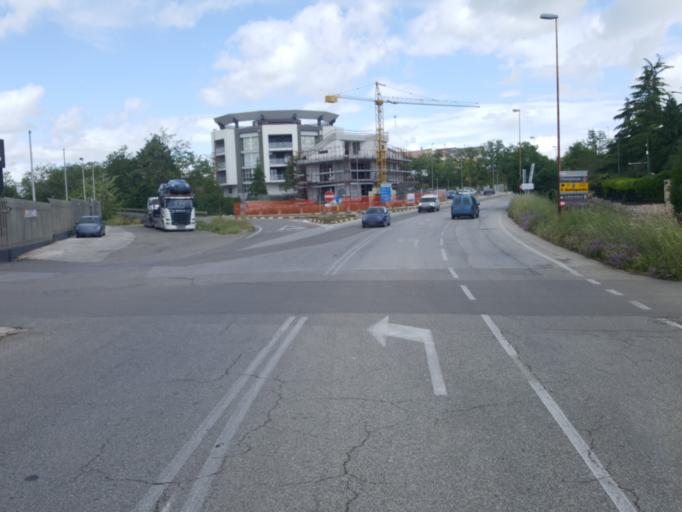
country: IT
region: Apulia
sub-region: Provincia di Bari
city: Altamura
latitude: 40.8132
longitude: 16.5542
